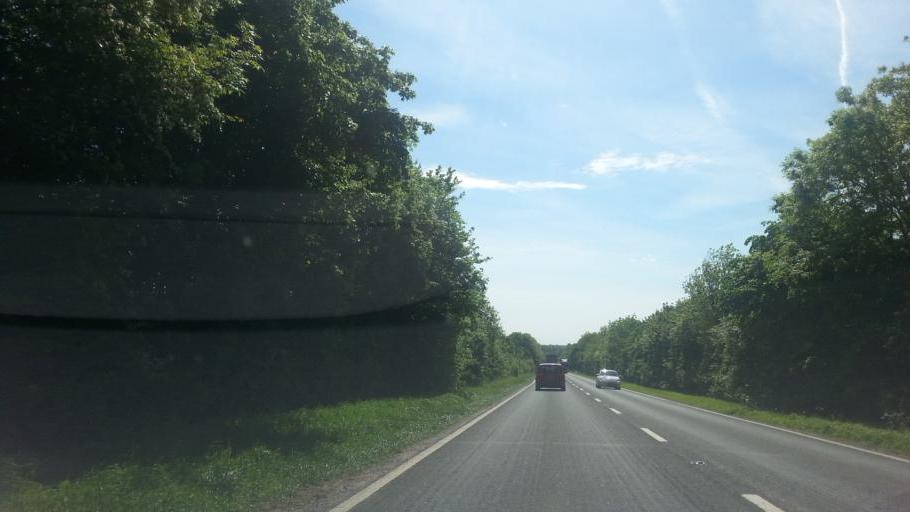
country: GB
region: England
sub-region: Cambridgeshire
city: Godmanchester
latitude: 52.3458
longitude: -0.1599
